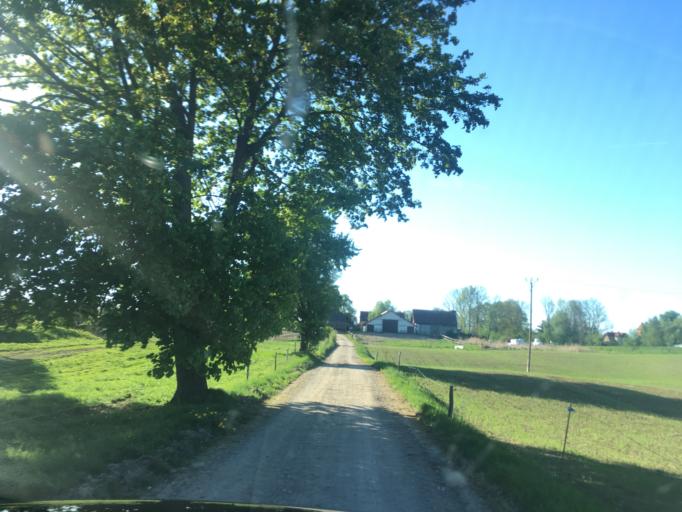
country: PL
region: Warmian-Masurian Voivodeship
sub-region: Powiat piski
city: Ruciane-Nida
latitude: 53.6613
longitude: 21.4789
